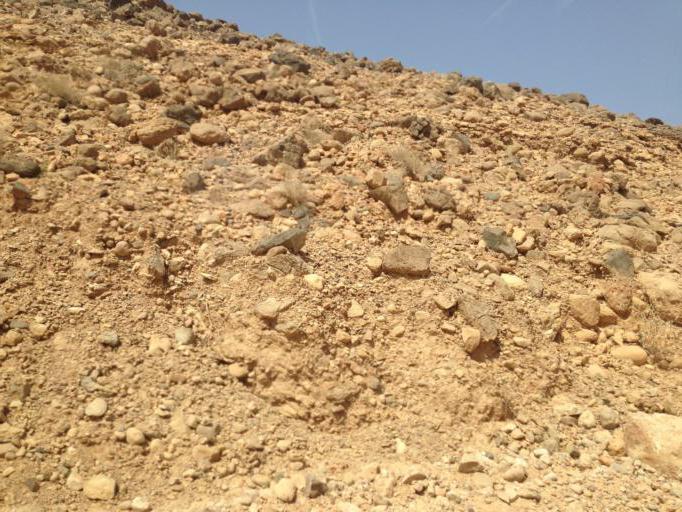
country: OM
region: Ash Sharqiyah
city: Ibra'
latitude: 23.0754
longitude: 58.8785
